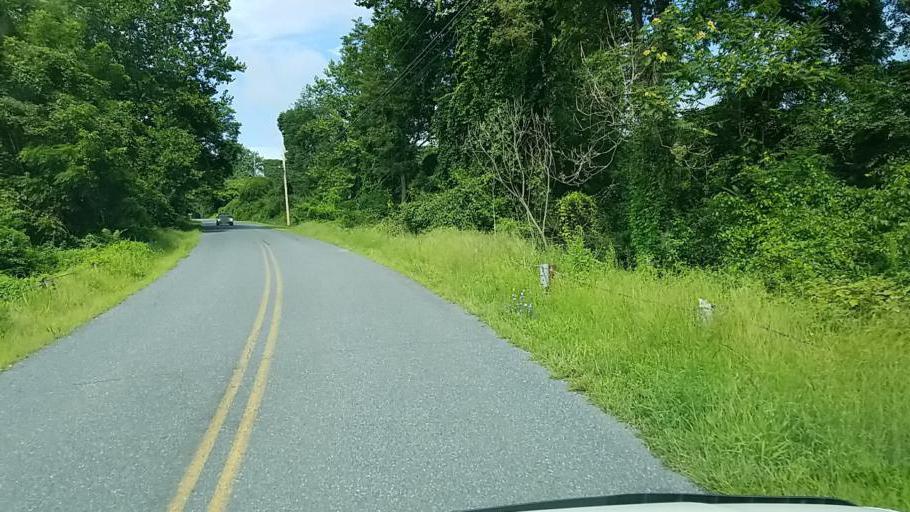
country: US
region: Pennsylvania
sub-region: Dauphin County
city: Millersburg
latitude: 40.5153
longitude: -76.9265
